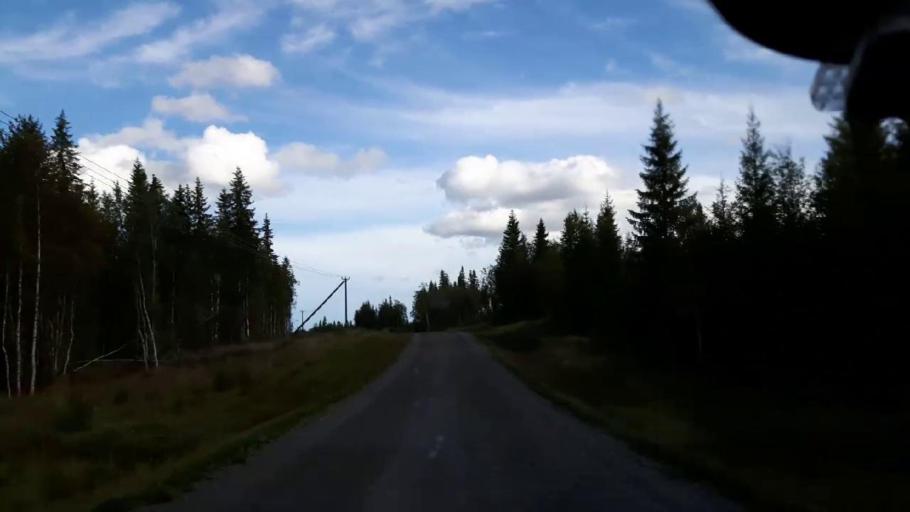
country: SE
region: Jaemtland
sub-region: Ragunda Kommun
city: Hammarstrand
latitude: 63.4400
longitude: 15.9898
